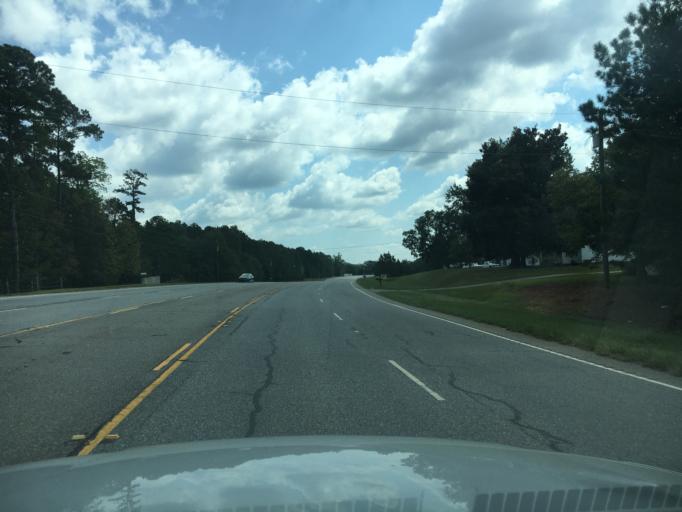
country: US
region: South Carolina
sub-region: Greenwood County
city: Ware Shoals
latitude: 34.4661
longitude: -82.2576
